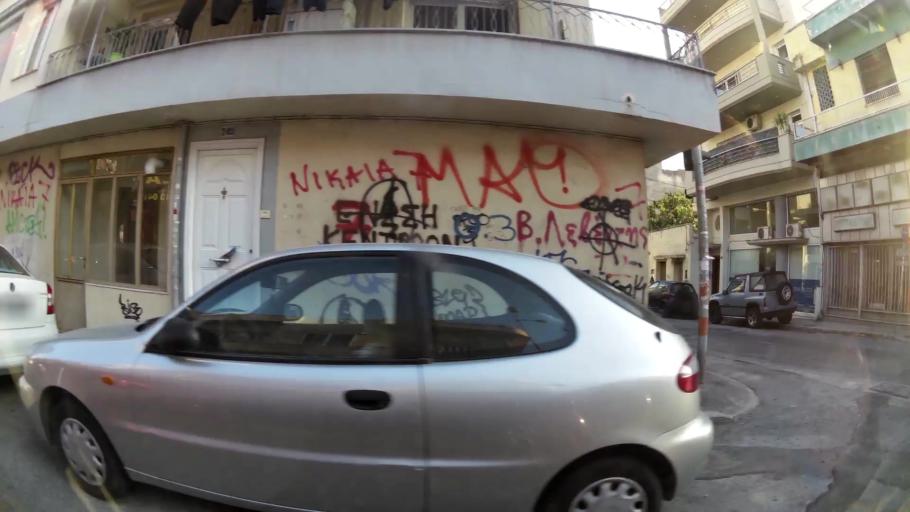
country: GR
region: Attica
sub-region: Nomos Piraios
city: Nikaia
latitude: 37.9692
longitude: 23.6487
